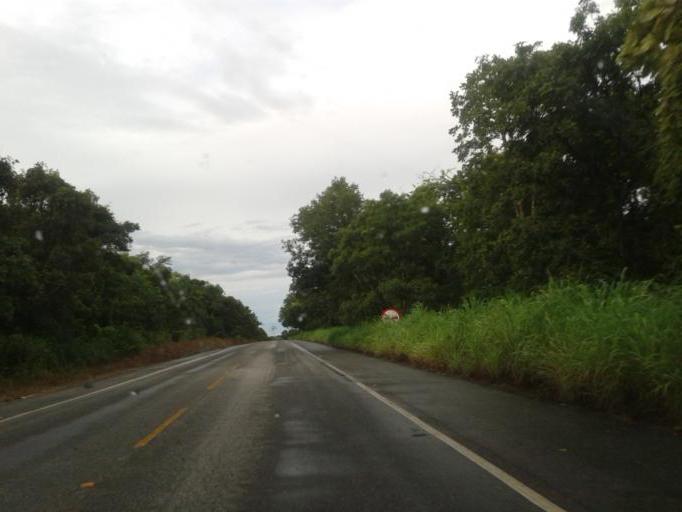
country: BR
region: Goias
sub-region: Mozarlandia
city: Mozarlandia
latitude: -14.8577
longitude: -50.5461
